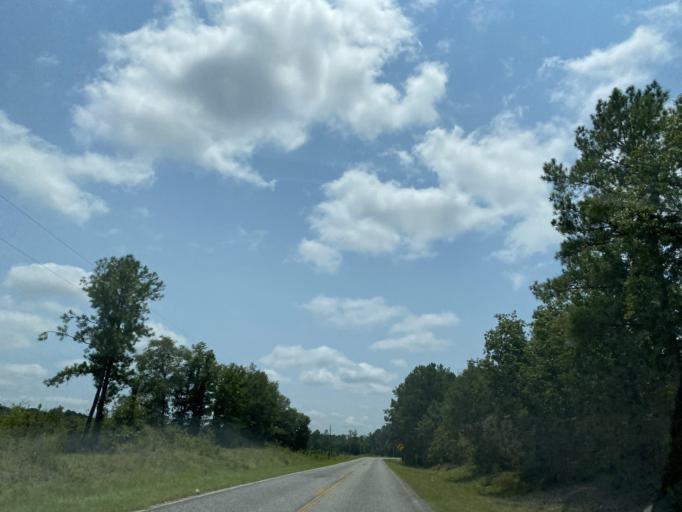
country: US
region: Georgia
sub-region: Telfair County
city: Lumber City
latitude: 31.9832
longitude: -82.7021
